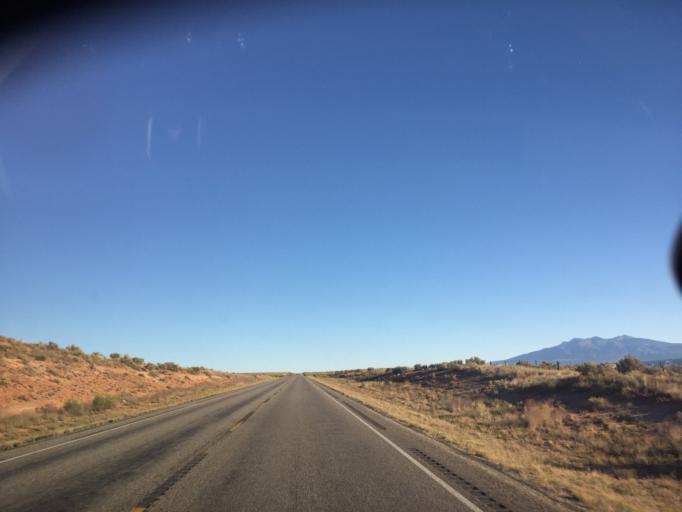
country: US
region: Utah
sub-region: San Juan County
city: Monticello
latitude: 38.1189
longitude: -109.3662
